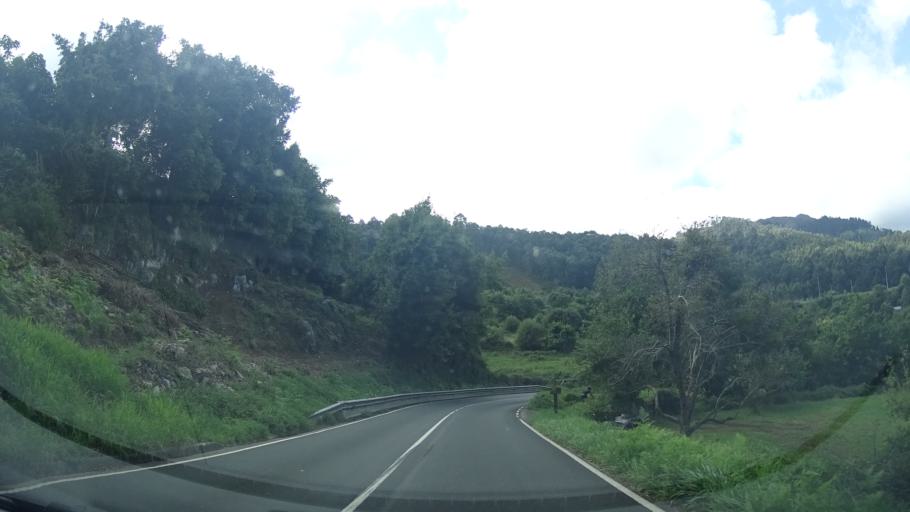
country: ES
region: Asturias
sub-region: Province of Asturias
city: Ribadesella
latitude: 43.4727
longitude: -5.1550
